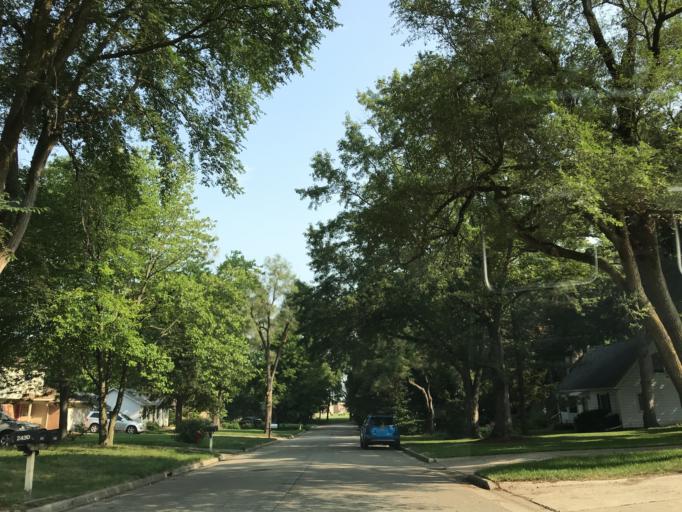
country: US
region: Michigan
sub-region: Washtenaw County
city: Ypsilanti
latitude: 42.2516
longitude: -83.6781
